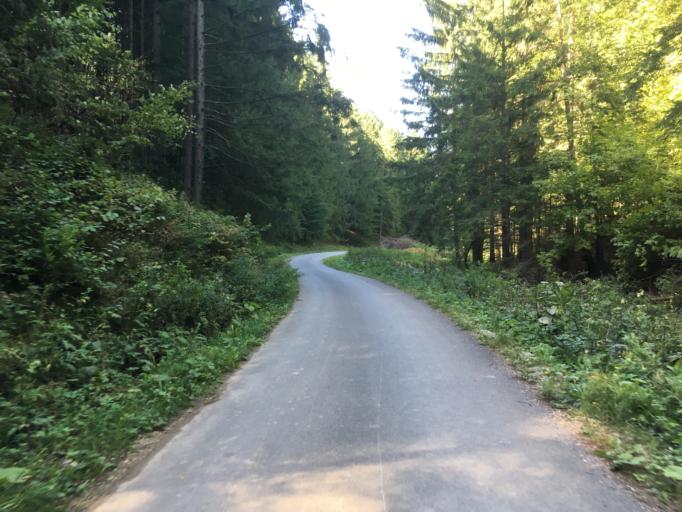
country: SK
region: Trenciansky
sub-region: Okres Povazska Bystrica
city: Povazska Bystrica
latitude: 49.0018
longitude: 18.4718
